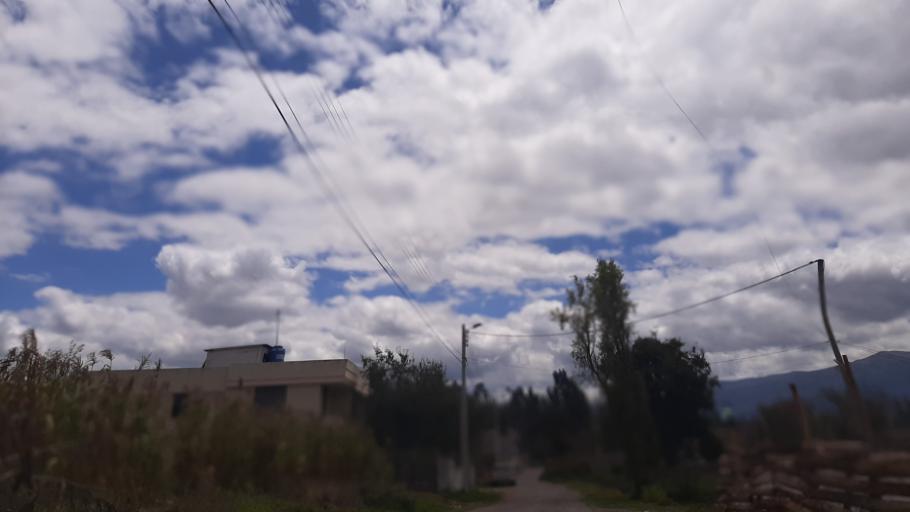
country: EC
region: Chimborazo
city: Riobamba
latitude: -1.6571
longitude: -78.6347
